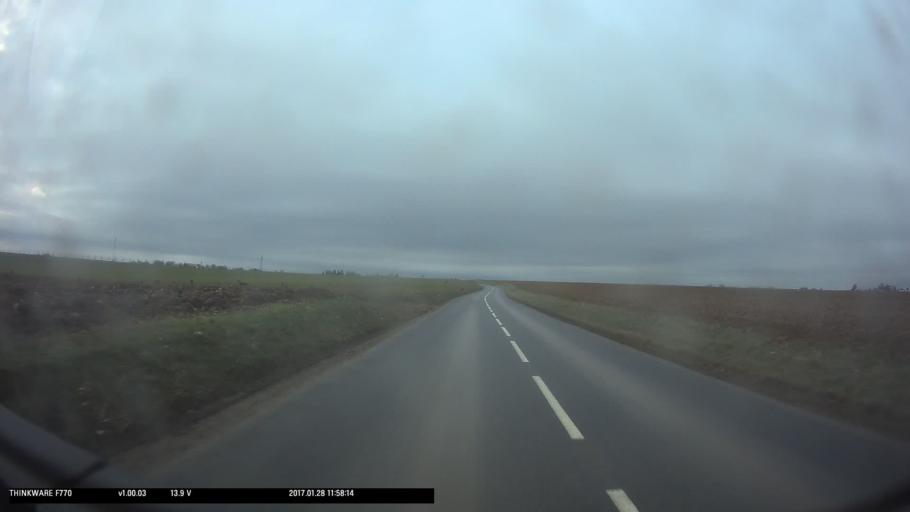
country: FR
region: Ile-de-France
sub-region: Departement du Val-d'Oise
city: Vigny
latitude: 49.0877
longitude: 1.9373
